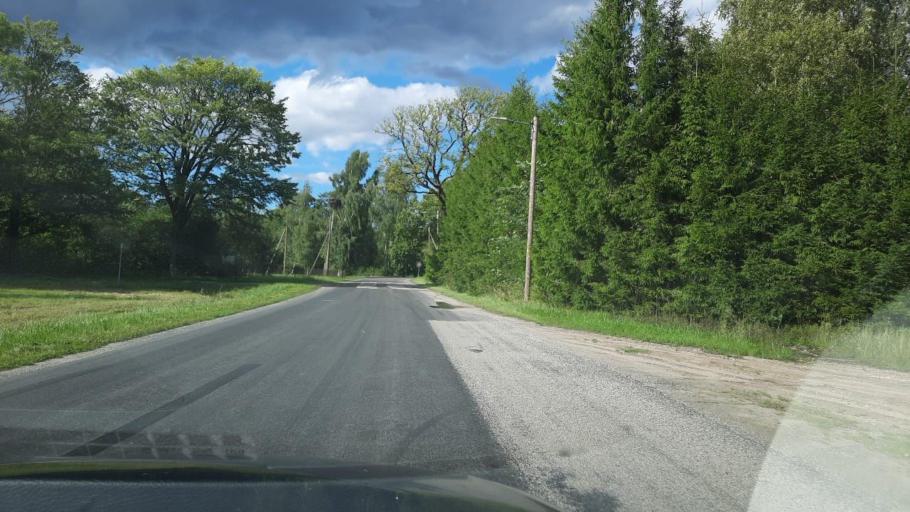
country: EE
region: Paernumaa
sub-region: Tootsi vald
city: Tootsi
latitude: 58.4914
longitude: 24.8971
